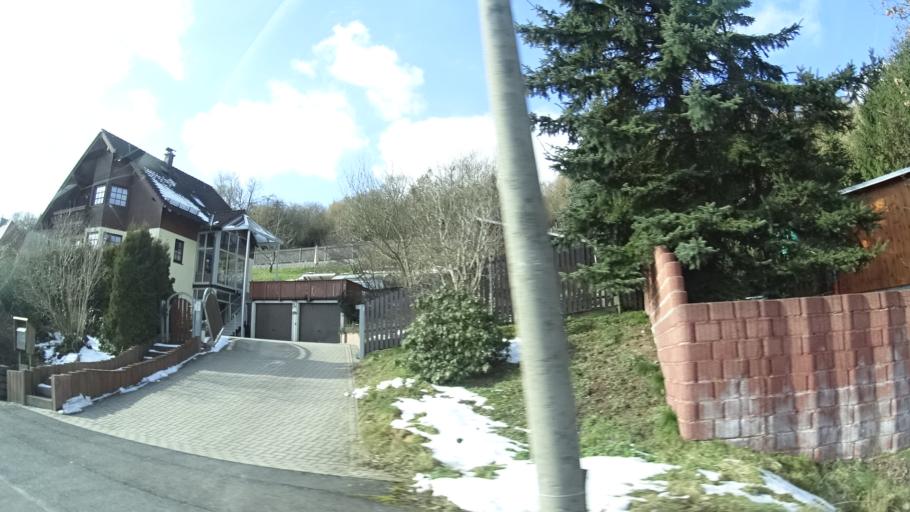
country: DE
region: Thuringia
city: Schwarza
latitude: 50.6112
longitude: 10.5234
